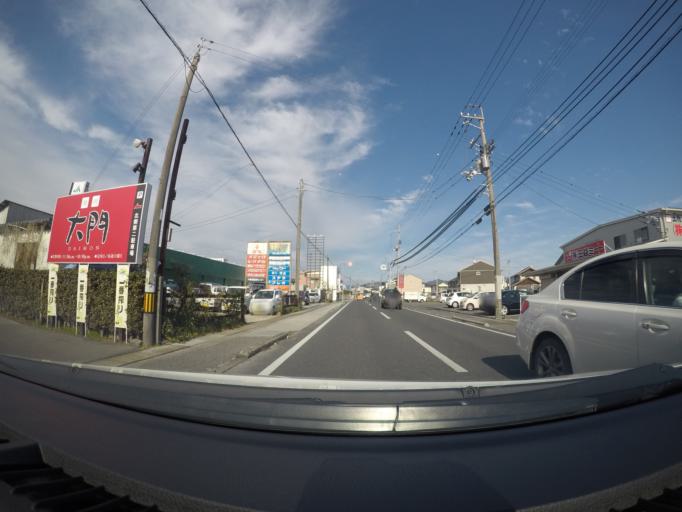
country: JP
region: Kochi
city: Kochi-shi
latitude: 33.6022
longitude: 133.6767
